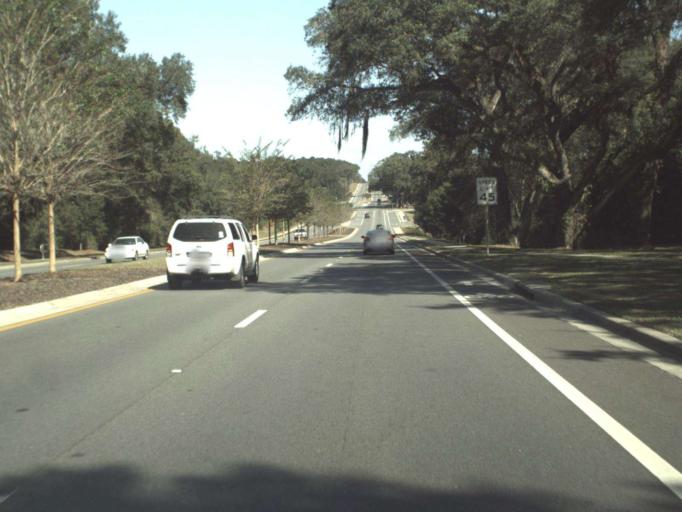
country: US
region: Florida
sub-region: Leon County
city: Tallahassee
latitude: 30.4749
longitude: -84.1867
